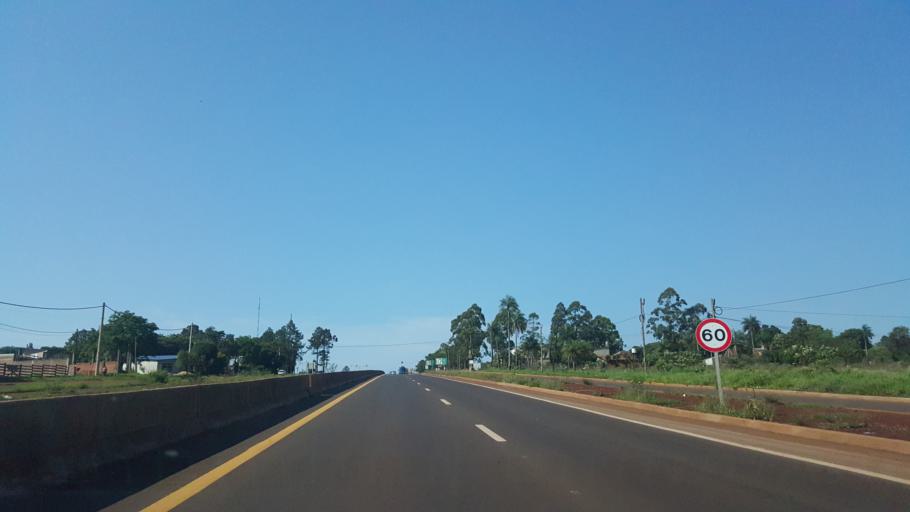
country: AR
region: Misiones
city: Garupa
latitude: -27.4671
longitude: -55.8631
